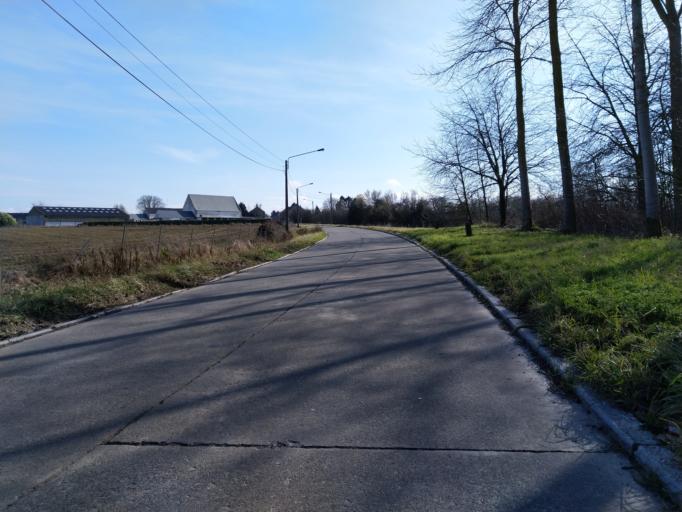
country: BE
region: Wallonia
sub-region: Province du Hainaut
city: Quevy-le-Petit
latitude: 50.3457
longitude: 3.8996
